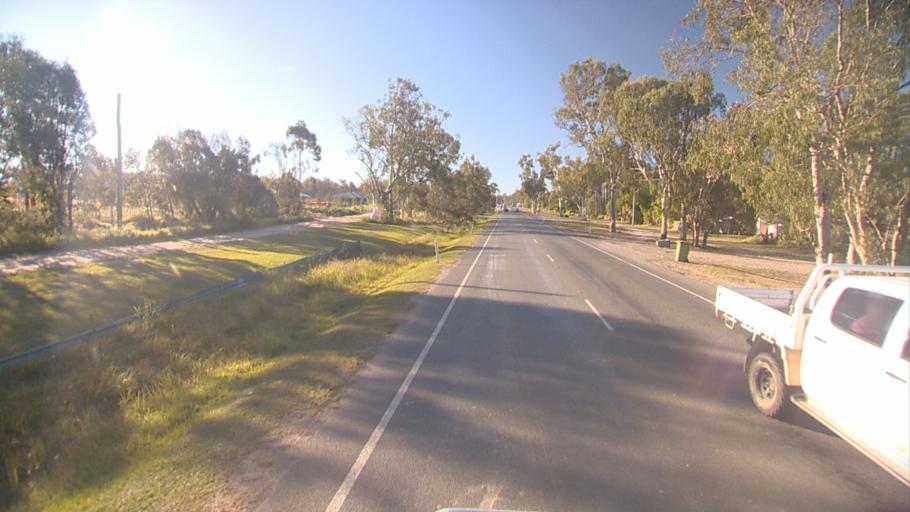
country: AU
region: Queensland
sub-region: Logan
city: Logan Reserve
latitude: -27.7144
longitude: 153.0927
